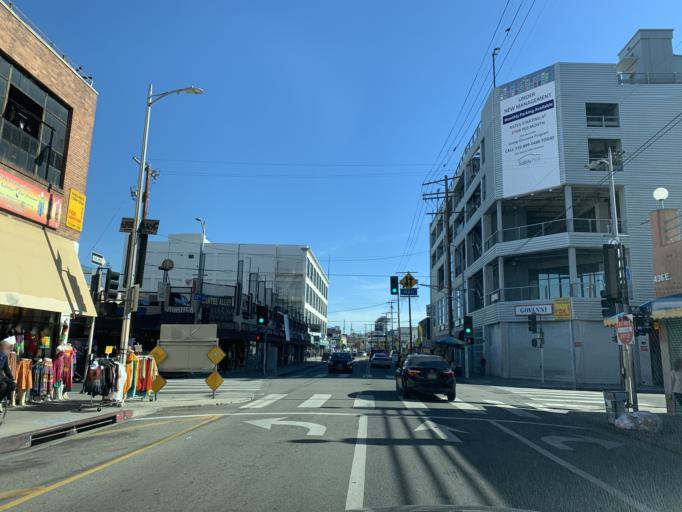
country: US
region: California
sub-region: Los Angeles County
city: Los Angeles
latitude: 34.0351
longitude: -118.2556
